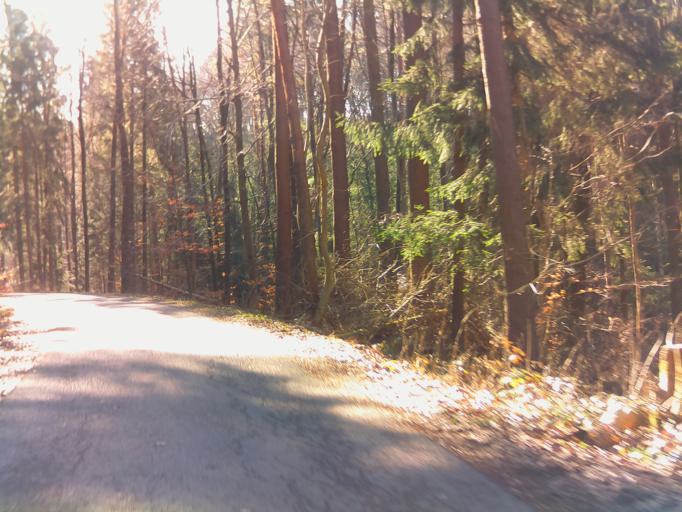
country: DE
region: Baden-Wuerttemberg
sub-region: Regierungsbezirk Stuttgart
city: Steinenbronn
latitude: 48.7080
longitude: 9.1029
